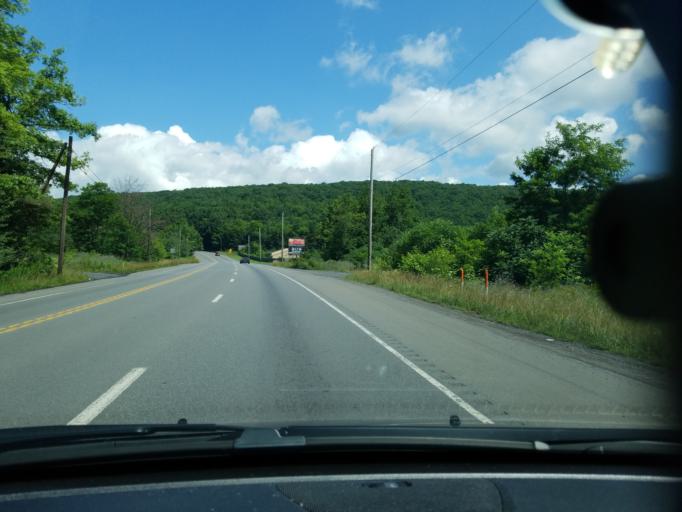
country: US
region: Pennsylvania
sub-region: Northumberland County
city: Mount Carmel
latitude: 40.8038
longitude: -76.4398
